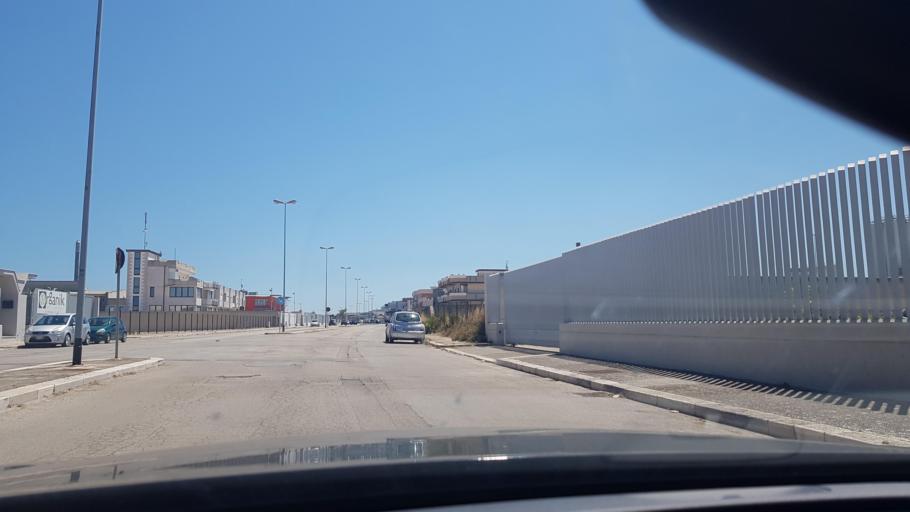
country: IT
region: Apulia
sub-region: Provincia di Barletta - Andria - Trani
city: Barletta
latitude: 41.3070
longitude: 16.3206
